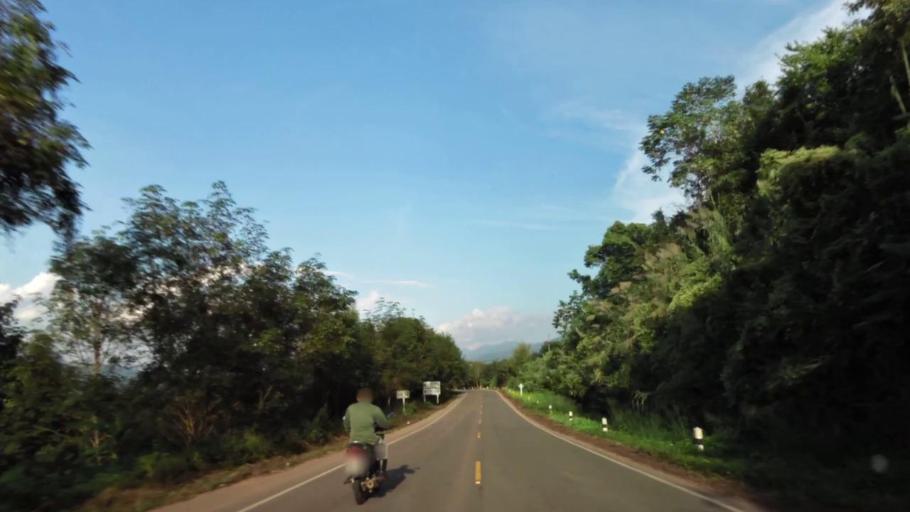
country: TH
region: Chiang Rai
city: Khun Tan
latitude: 19.8541
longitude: 100.3851
